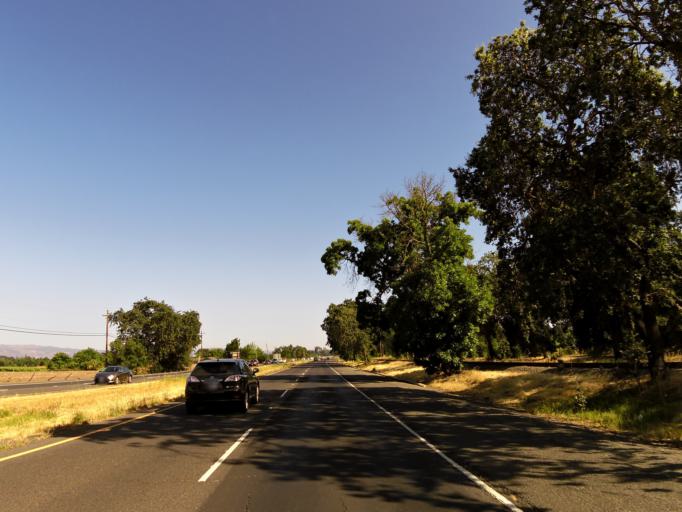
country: US
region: California
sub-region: Napa County
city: Yountville
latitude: 38.3900
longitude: -122.3523
